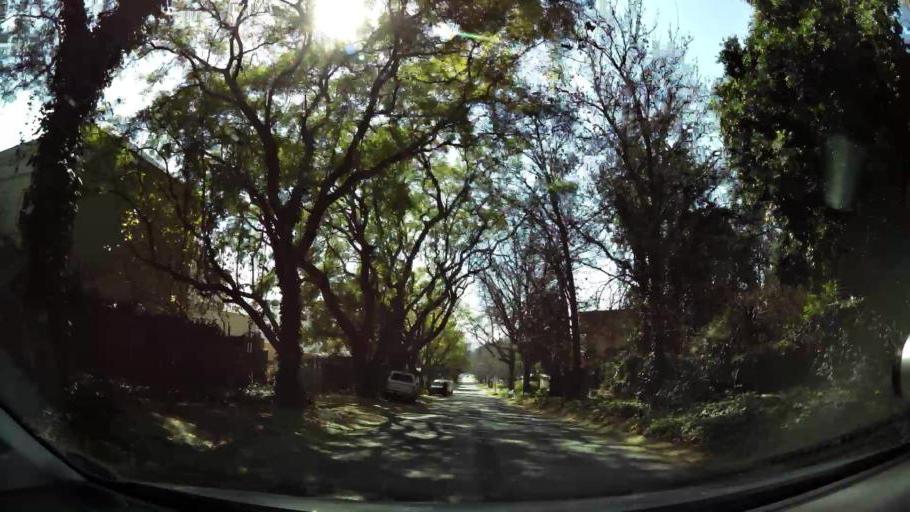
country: ZA
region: Gauteng
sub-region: City of Johannesburg Metropolitan Municipality
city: Modderfontein
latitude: -26.1608
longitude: 28.1228
